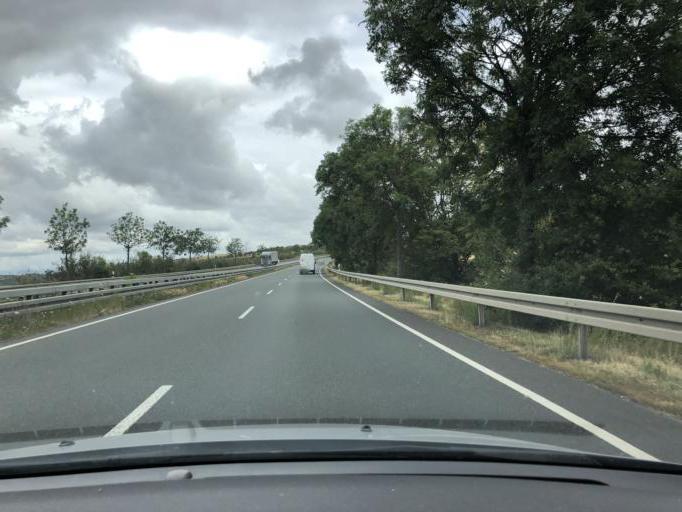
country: DE
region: Saxony-Anhalt
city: Hohnstedt
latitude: 51.4771
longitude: 11.7141
